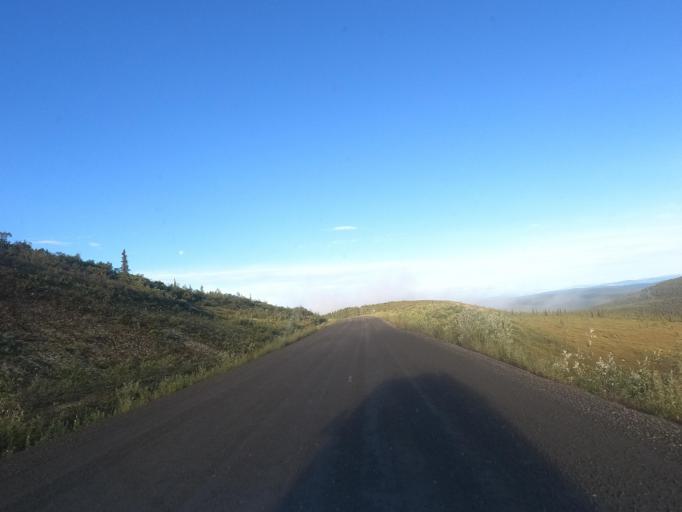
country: CA
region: Yukon
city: Dawson City
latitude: 64.2205
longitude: -140.3085
